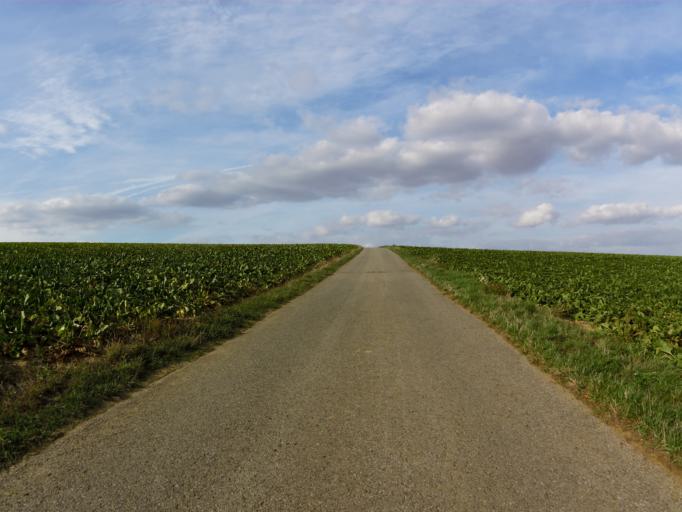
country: DE
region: Bavaria
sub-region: Regierungsbezirk Unterfranken
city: Reichenberg
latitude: 49.7112
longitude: 9.9482
